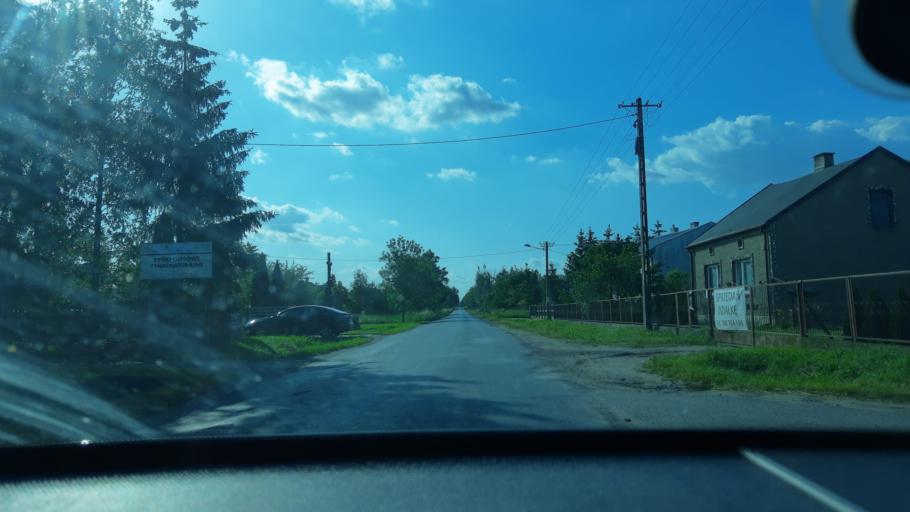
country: PL
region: Lodz Voivodeship
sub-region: Powiat sieradzki
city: Sieradz
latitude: 51.5486
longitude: 18.7755
